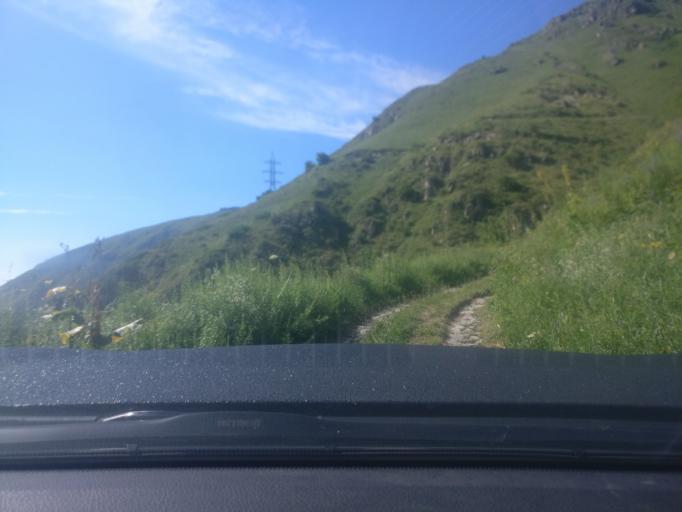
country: KZ
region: Almaty Qalasy
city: Almaty
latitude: 43.0966
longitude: 76.9550
